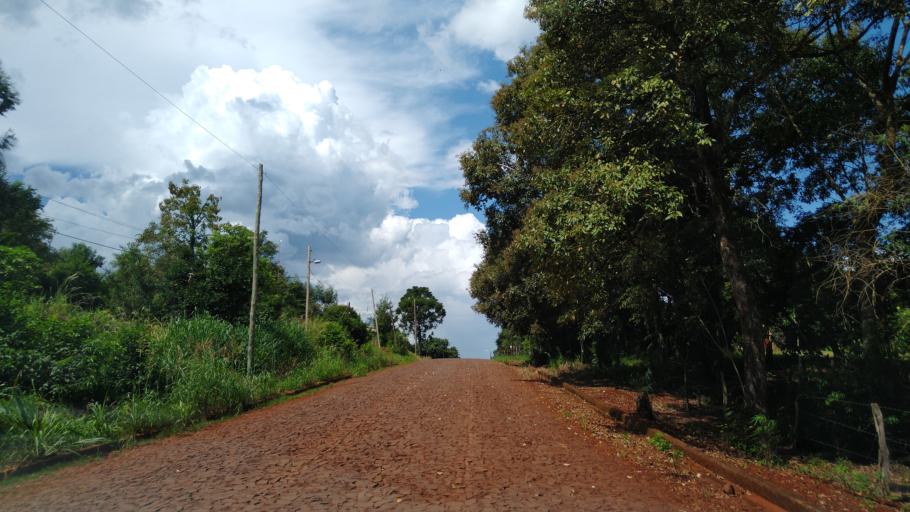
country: AR
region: Misiones
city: Puerto Libertad
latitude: -25.9661
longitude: -54.5985
